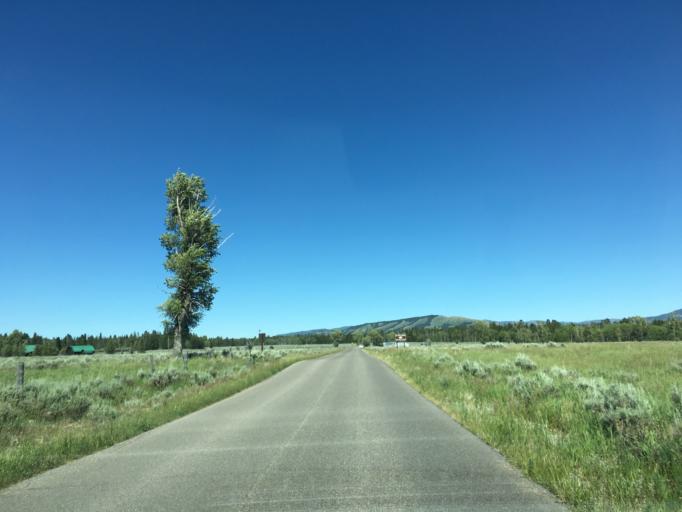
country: US
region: Wyoming
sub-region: Teton County
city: Moose Wilson Road
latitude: 43.5981
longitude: -110.8014
